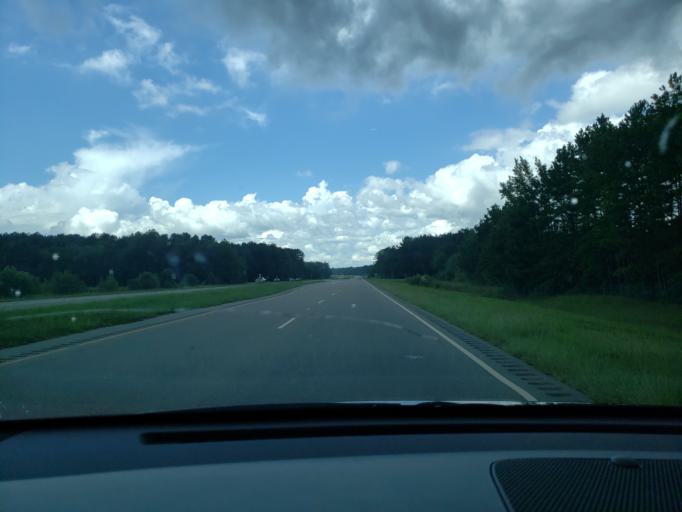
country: US
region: North Carolina
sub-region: Bladen County
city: Elizabethtown
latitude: 34.6239
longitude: -78.6496
